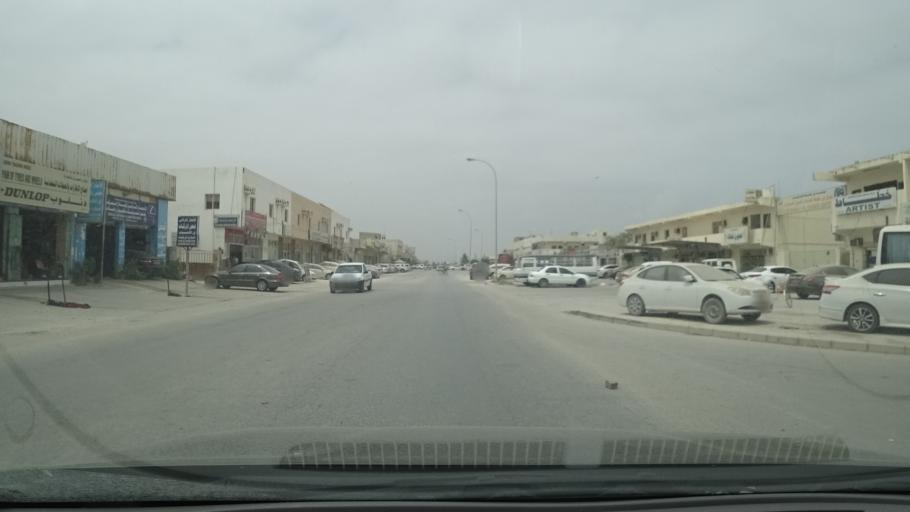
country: OM
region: Zufar
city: Salalah
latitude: 17.0228
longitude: 54.0492
